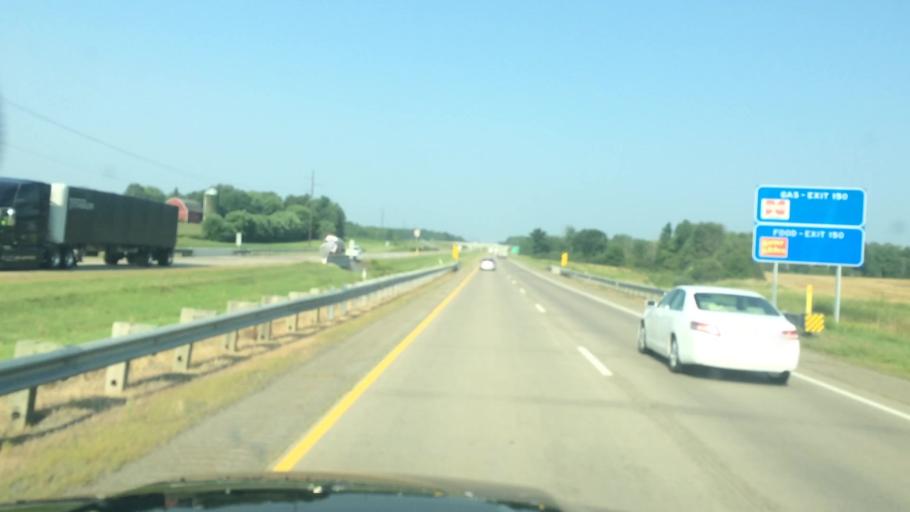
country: US
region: Wisconsin
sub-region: Marathon County
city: Edgar
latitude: 44.9446
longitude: -89.9504
